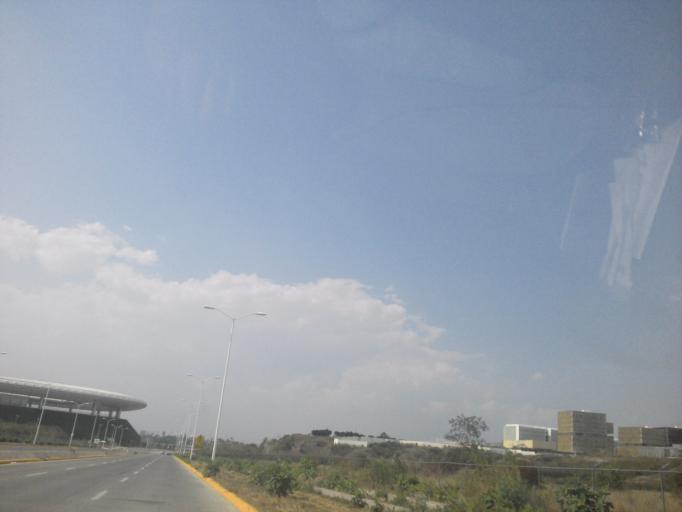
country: MX
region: Jalisco
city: Guadalajara
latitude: 20.6761
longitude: -103.4616
